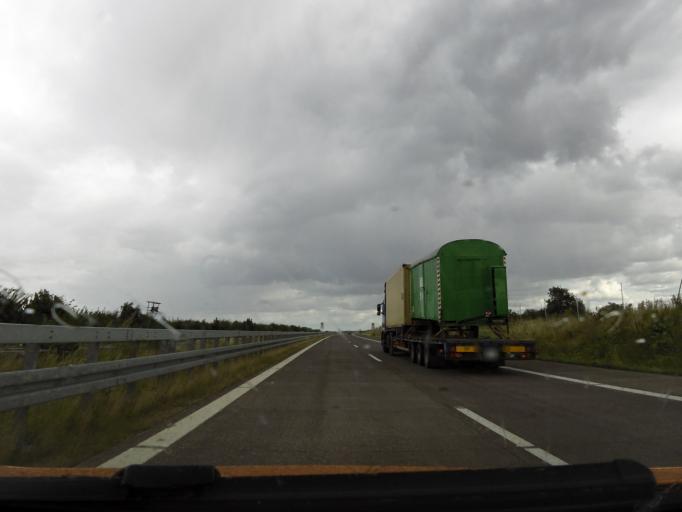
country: DE
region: Brandenburg
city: Gramzow
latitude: 53.2758
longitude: 14.0599
